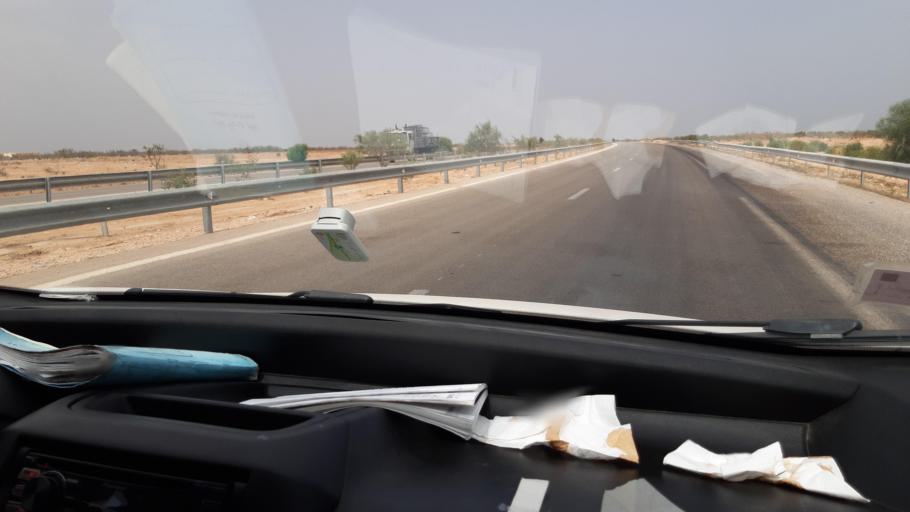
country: TN
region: Safaqis
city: Sfax
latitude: 34.8437
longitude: 10.6718
